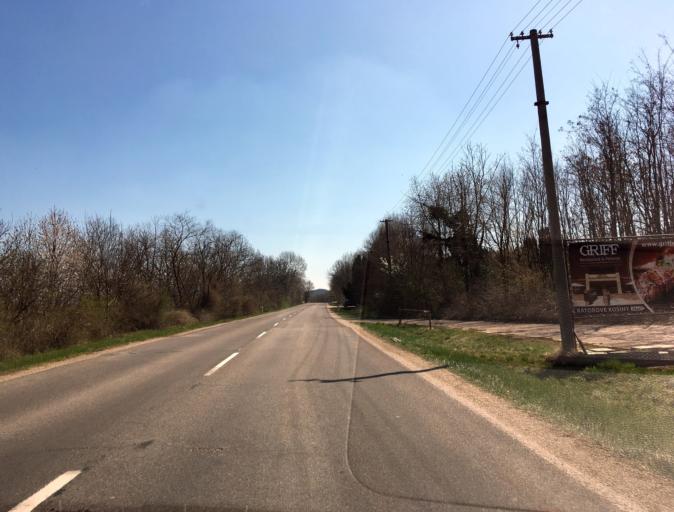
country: SK
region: Nitriansky
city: Svodin
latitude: 47.8712
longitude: 18.4557
